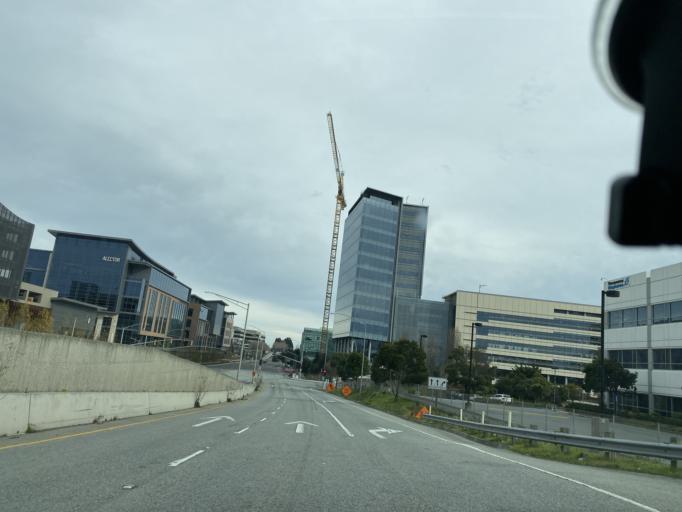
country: US
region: California
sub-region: San Mateo County
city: South San Francisco
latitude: 37.6620
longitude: -122.3977
